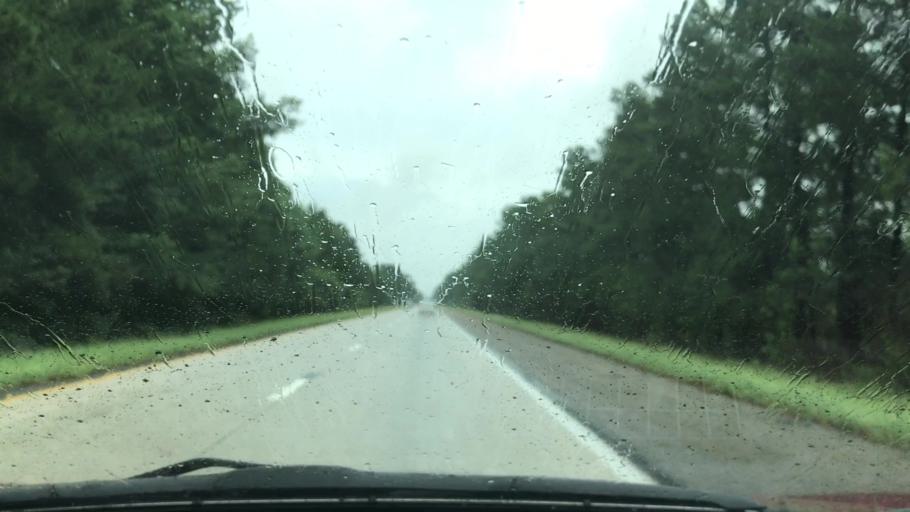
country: US
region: South Carolina
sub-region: Orangeburg County
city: Holly Hill
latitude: 33.2077
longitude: -80.4085
